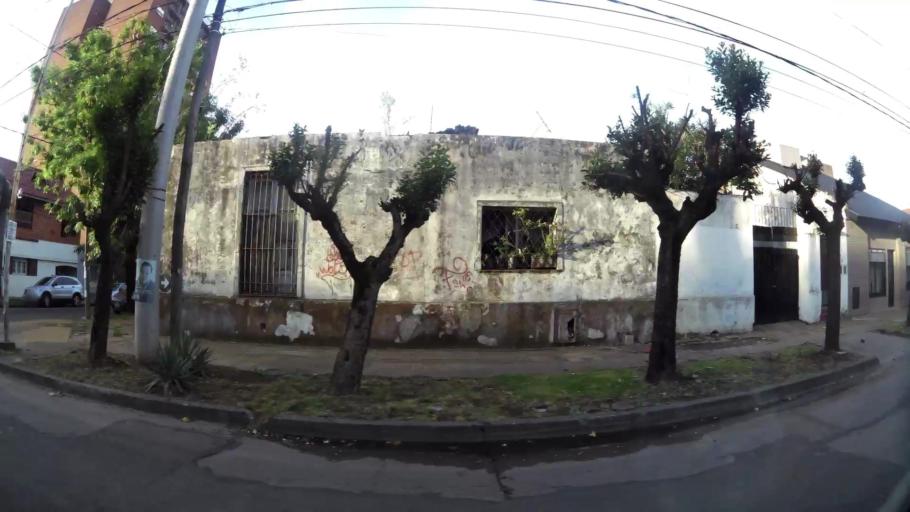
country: AR
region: Buenos Aires
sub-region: Partido de Moron
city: Moron
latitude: -34.6548
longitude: -58.6161
